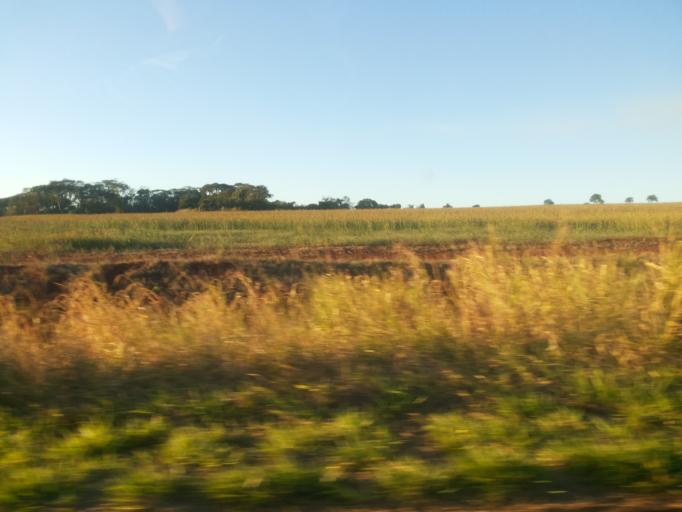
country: BR
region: Minas Gerais
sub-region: Centralina
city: Centralina
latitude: -18.7324
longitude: -49.2567
